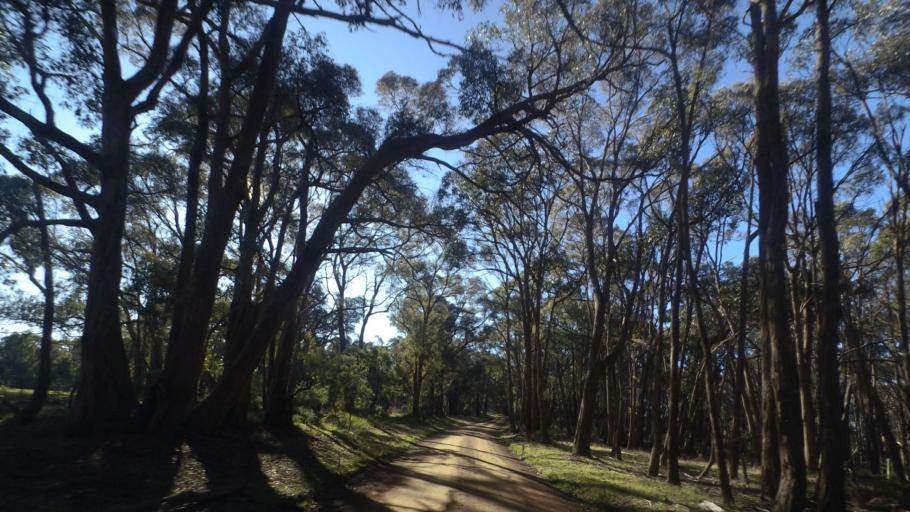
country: AU
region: Victoria
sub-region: Mount Alexander
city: Castlemaine
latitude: -37.2795
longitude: 144.3364
